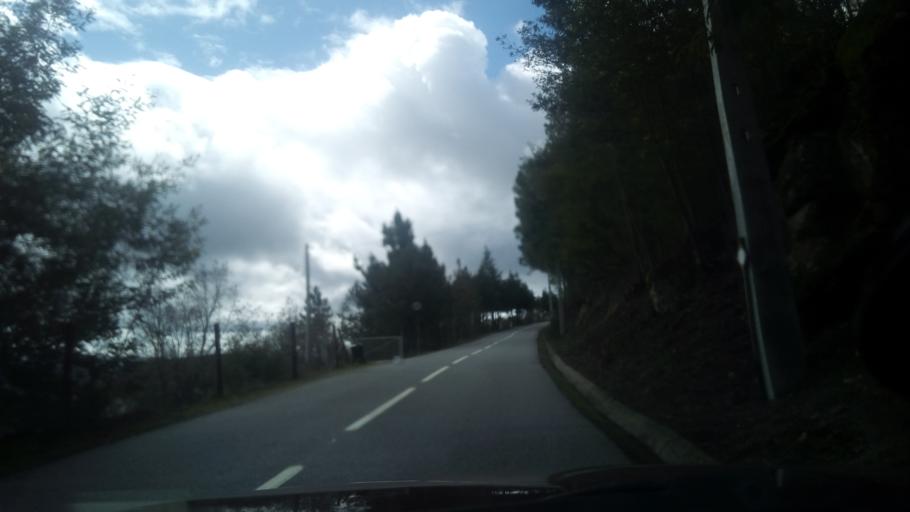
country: PT
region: Guarda
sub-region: Fornos de Algodres
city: Fornos de Algodres
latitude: 40.6179
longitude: -7.4819
